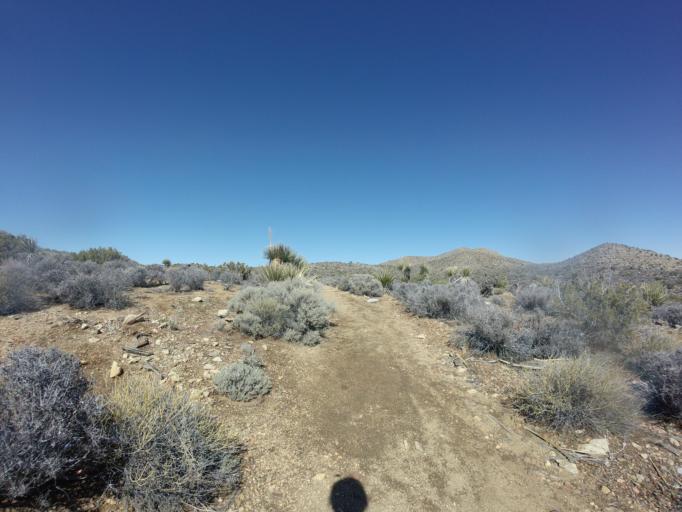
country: US
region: California
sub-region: Riverside County
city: Sky Valley
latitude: 33.9280
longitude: -116.1390
